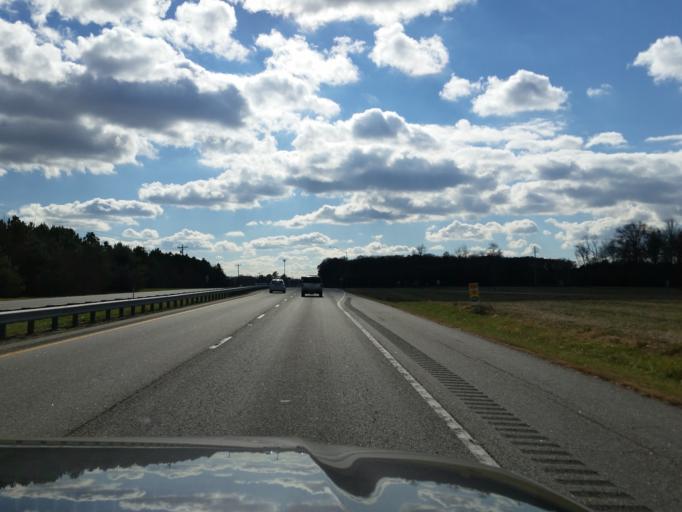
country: US
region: Maryland
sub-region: Queen Anne's County
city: Centreville
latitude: 38.9077
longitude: -76.0621
